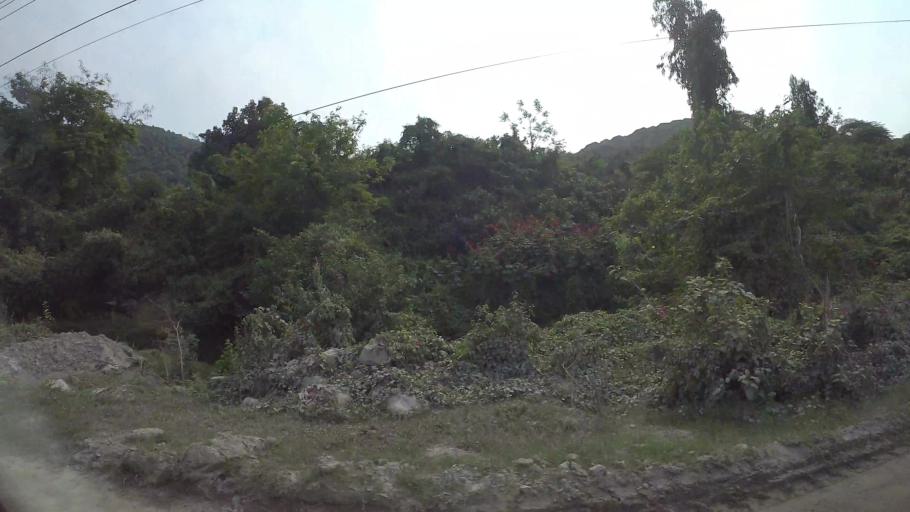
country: VN
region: Da Nang
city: Lien Chieu
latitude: 16.0398
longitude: 108.1517
